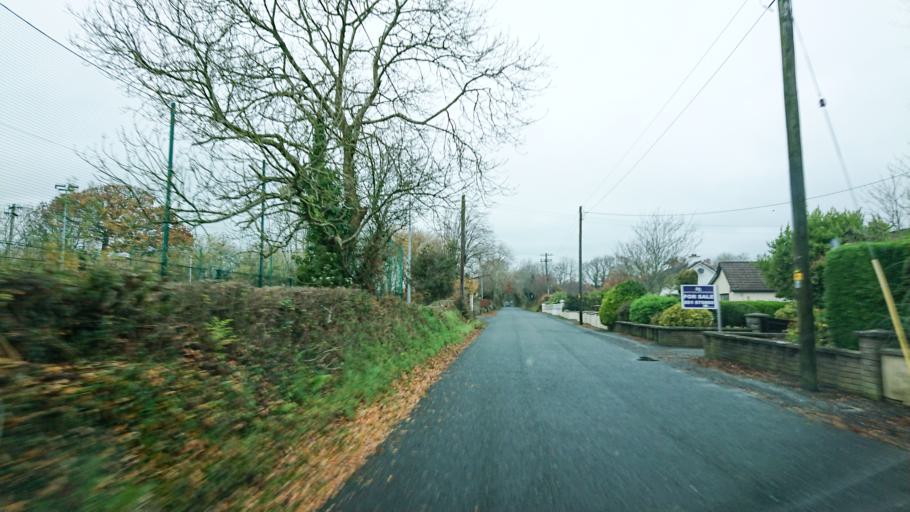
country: IE
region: Munster
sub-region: Waterford
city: Waterford
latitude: 52.2398
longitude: -7.1800
